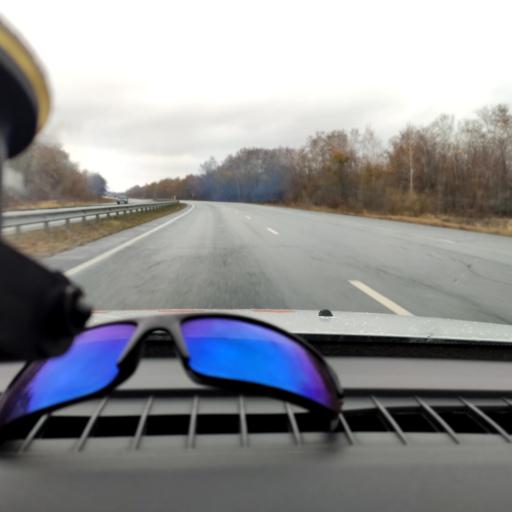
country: RU
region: Samara
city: Novokuybyshevsk
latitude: 53.0282
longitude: 49.9925
